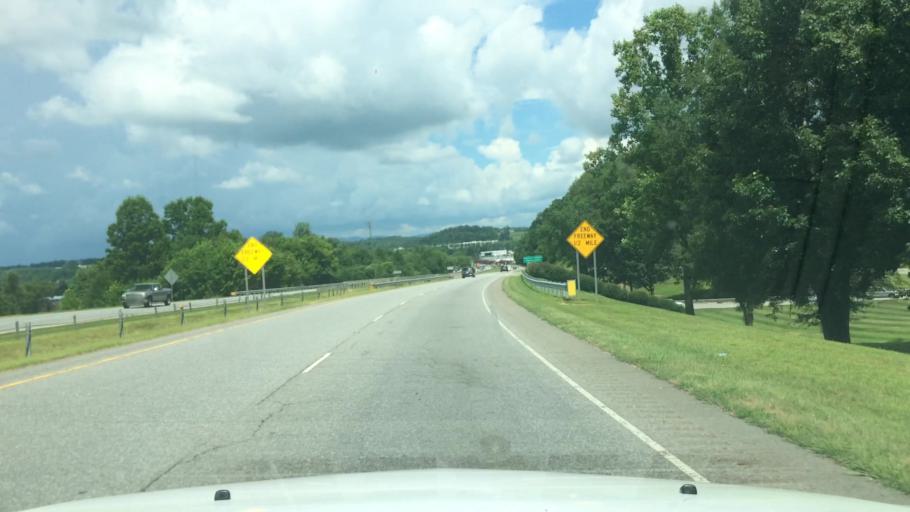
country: US
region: North Carolina
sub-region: Wilkes County
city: Wilkesboro
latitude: 36.1399
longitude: -81.1724
